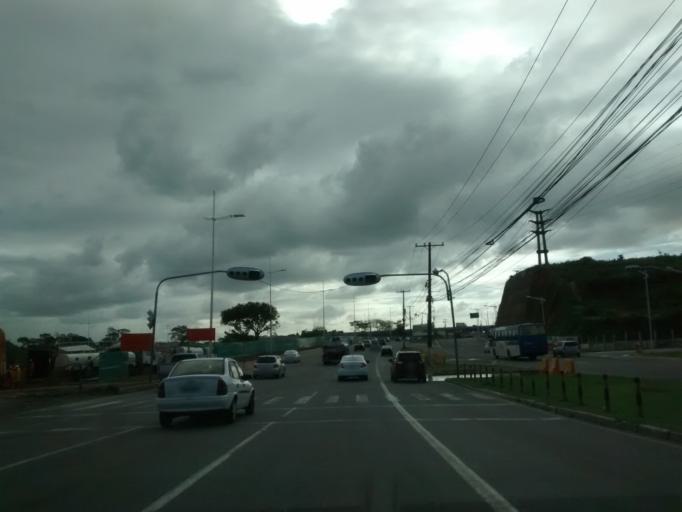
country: BR
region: Bahia
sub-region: Lauro De Freitas
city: Lauro de Freitas
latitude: -12.9279
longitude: -38.3857
